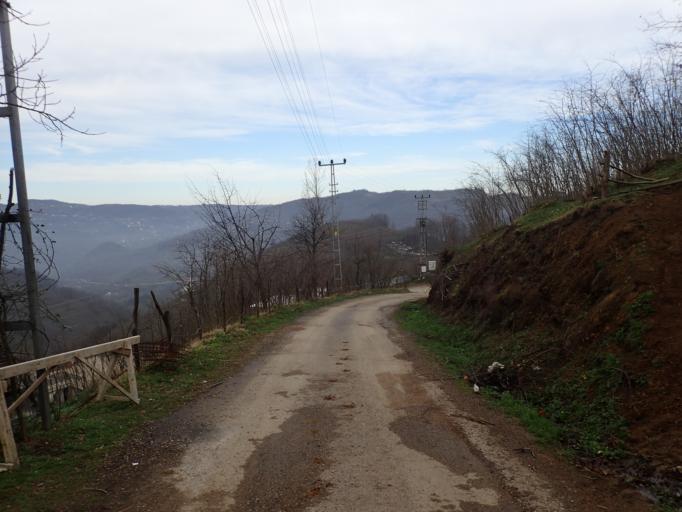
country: TR
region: Ordu
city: Camas
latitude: 40.8895
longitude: 37.5117
